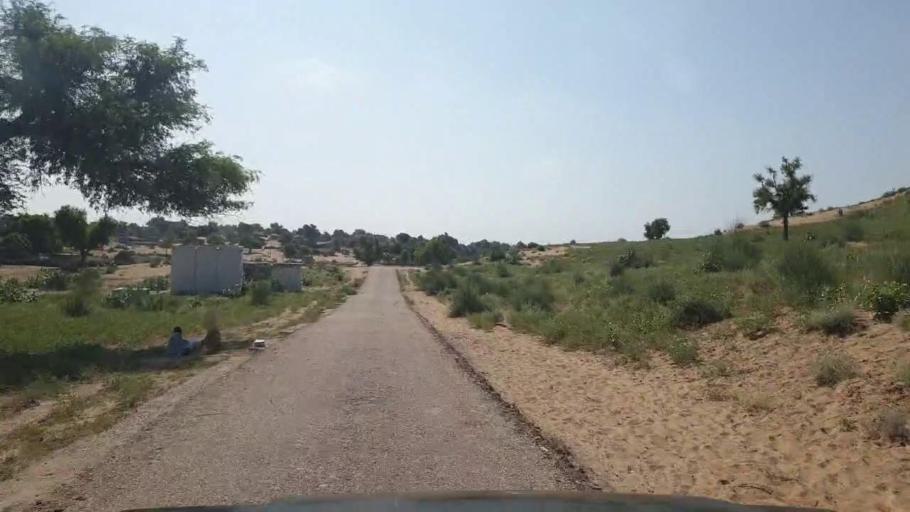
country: PK
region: Sindh
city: Islamkot
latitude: 25.1586
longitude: 70.4092
